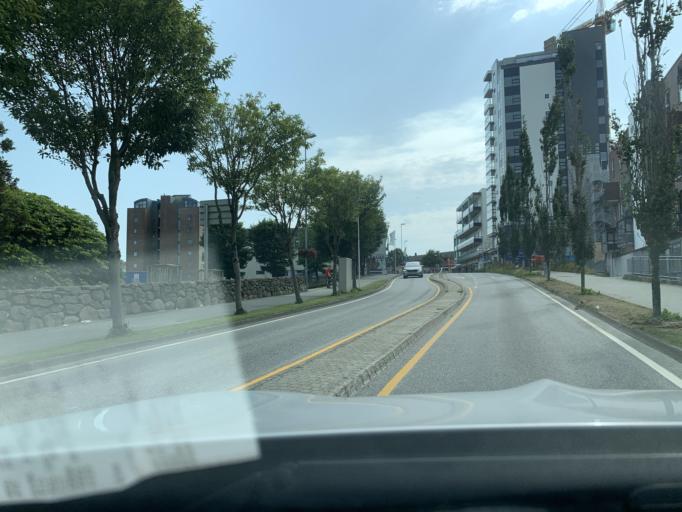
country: NO
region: Rogaland
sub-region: Klepp
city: Kleppe
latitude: 58.7758
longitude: 5.6302
